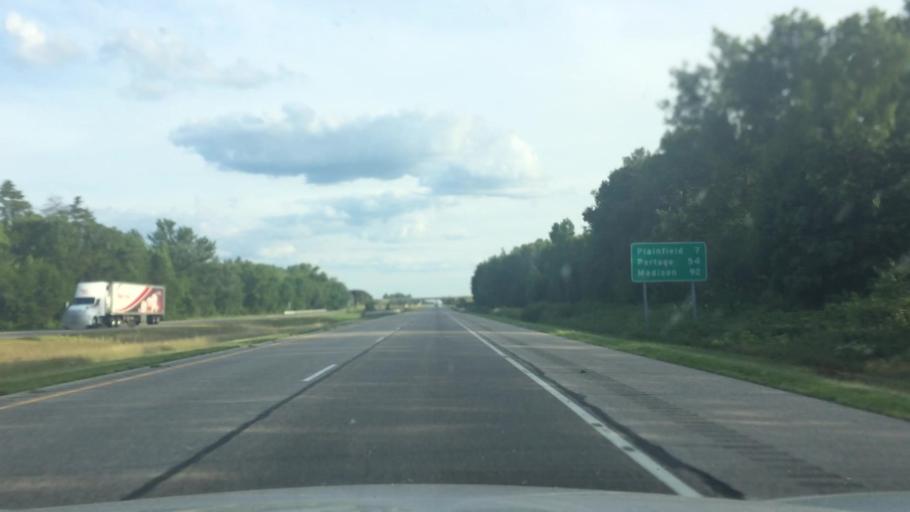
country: US
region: Wisconsin
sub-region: Portage County
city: Plover
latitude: 44.2954
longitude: -89.5237
